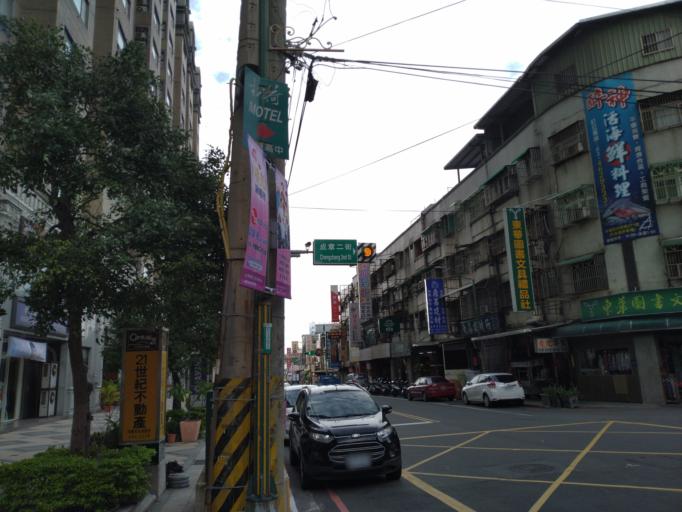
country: TW
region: Taiwan
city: Taoyuan City
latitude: 24.9784
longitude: 121.2511
